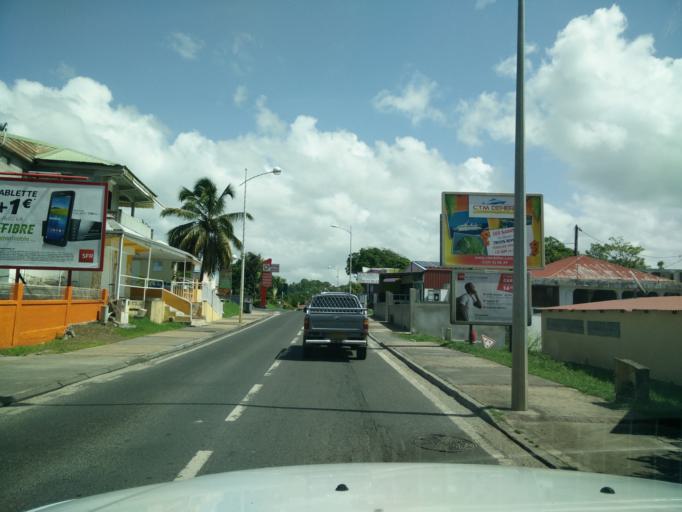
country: GP
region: Guadeloupe
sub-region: Guadeloupe
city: Le Gosier
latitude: 16.2100
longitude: -61.5002
